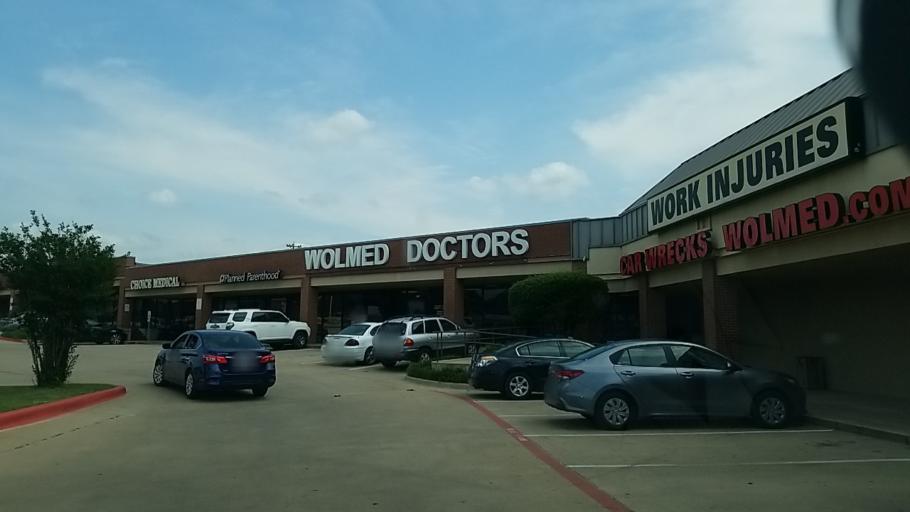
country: US
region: Texas
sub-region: Denton County
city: Denton
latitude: 33.1834
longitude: -97.1065
